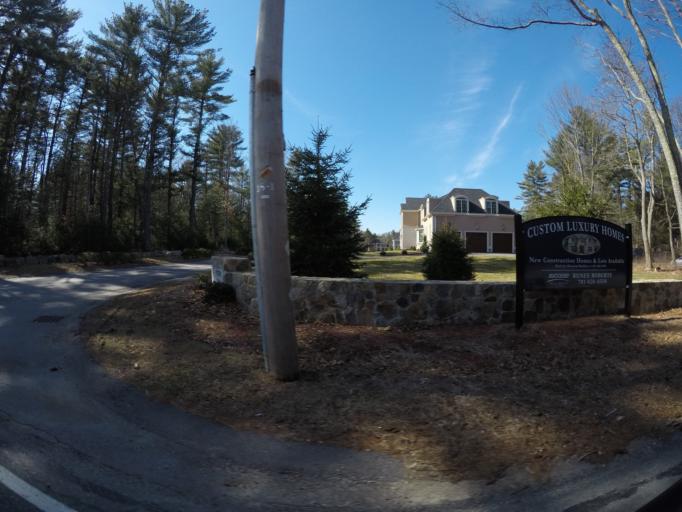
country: US
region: Massachusetts
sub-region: Bristol County
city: Easton
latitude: 42.0705
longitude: -71.1379
